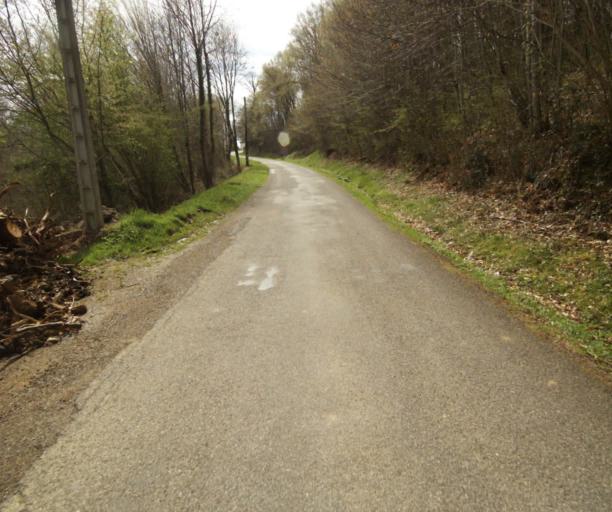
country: FR
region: Limousin
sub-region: Departement de la Correze
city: Laguenne
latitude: 45.2377
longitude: 1.8400
